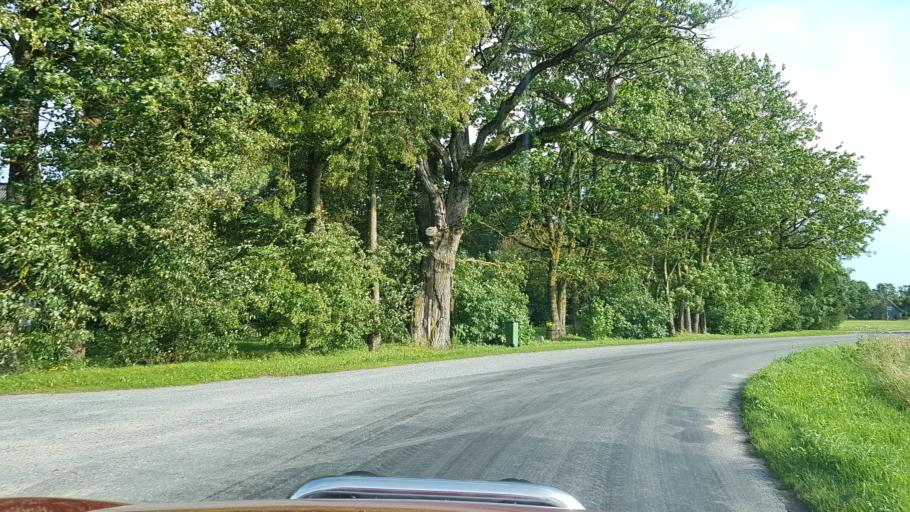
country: EE
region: Laeaene
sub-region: Lihula vald
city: Lihula
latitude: 58.4480
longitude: 24.0015
